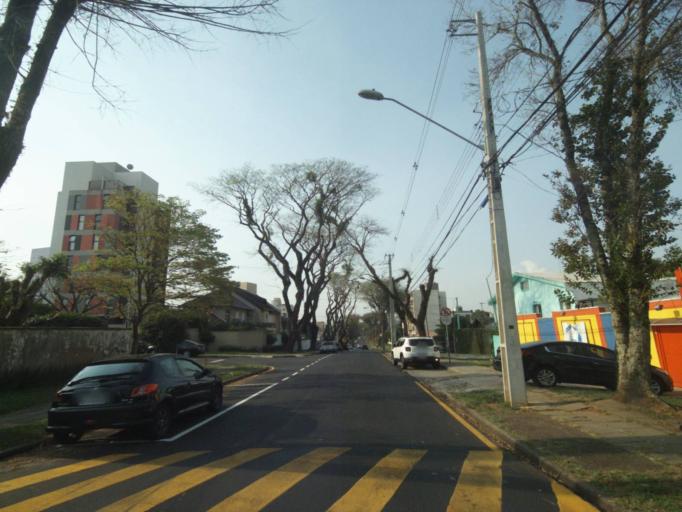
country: BR
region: Parana
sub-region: Curitiba
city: Curitiba
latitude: -25.4647
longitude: -49.2988
